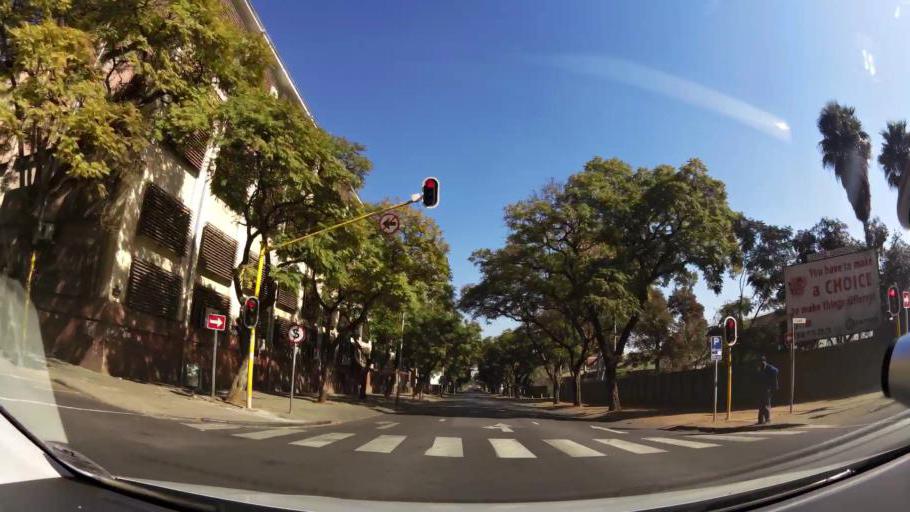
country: ZA
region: Gauteng
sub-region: City of Tshwane Metropolitan Municipality
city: Pretoria
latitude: -25.7437
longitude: 28.1853
